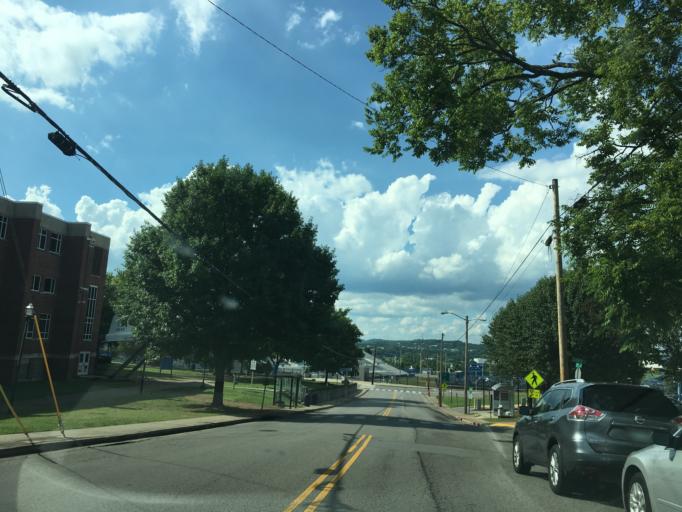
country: US
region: Tennessee
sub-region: Davidson County
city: Nashville
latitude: 36.1660
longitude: -86.8267
